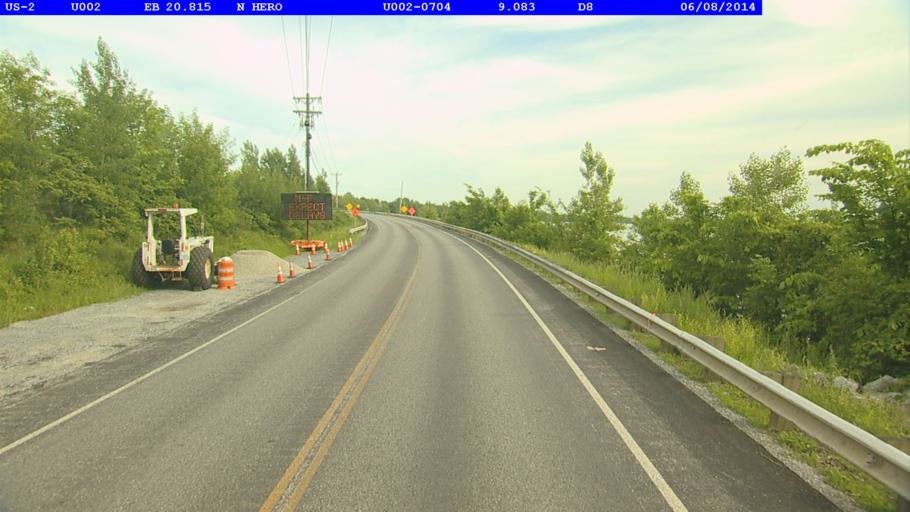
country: US
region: Vermont
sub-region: Grand Isle County
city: North Hero
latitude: 44.7692
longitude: -73.2929
